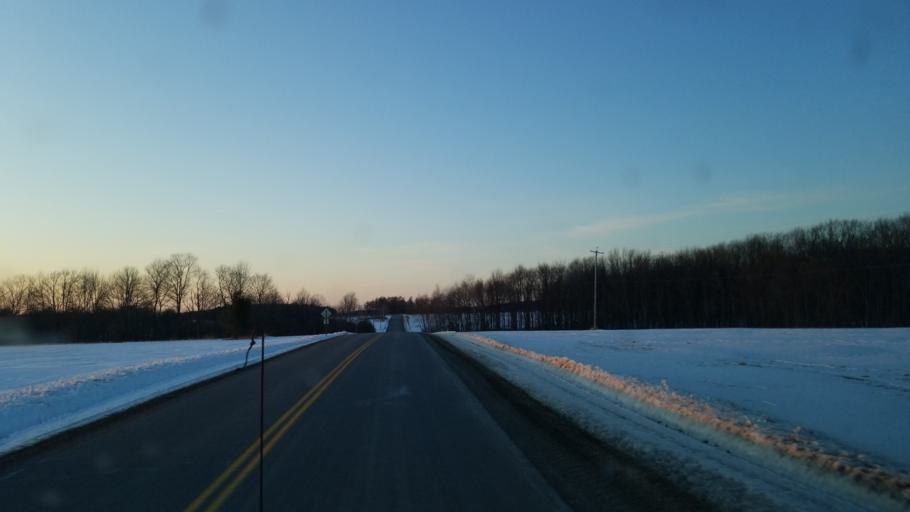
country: US
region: Pennsylvania
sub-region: Tioga County
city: Westfield
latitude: 42.0017
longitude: -77.6916
